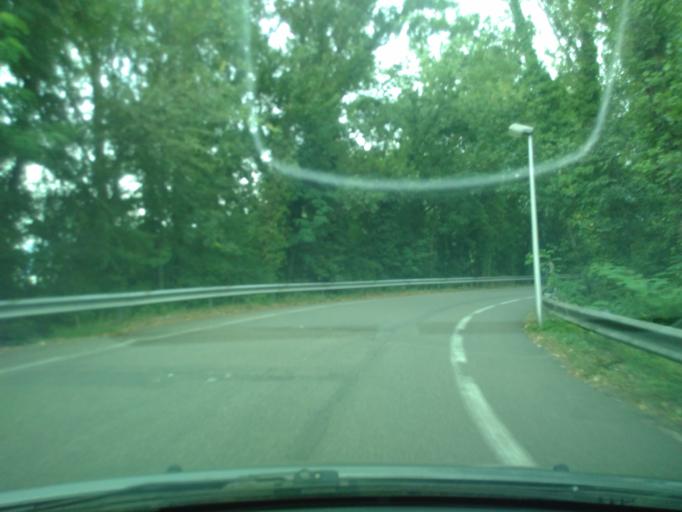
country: FR
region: Rhone-Alpes
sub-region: Departement de l'Isere
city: Corenc
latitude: 45.2034
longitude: 5.7699
